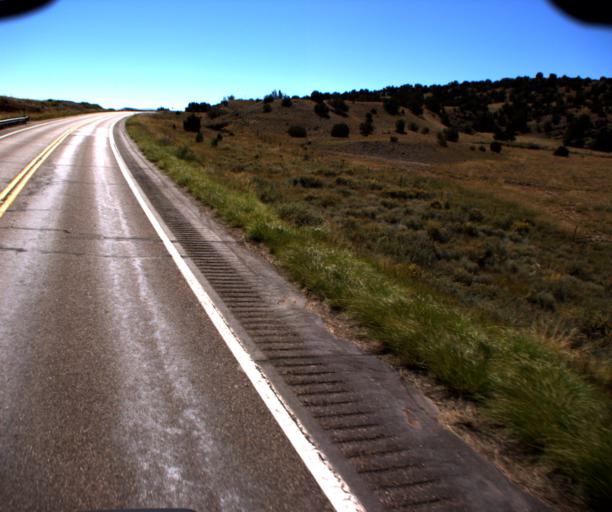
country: US
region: Arizona
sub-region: Apache County
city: Saint Johns
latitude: 34.3584
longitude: -109.3811
